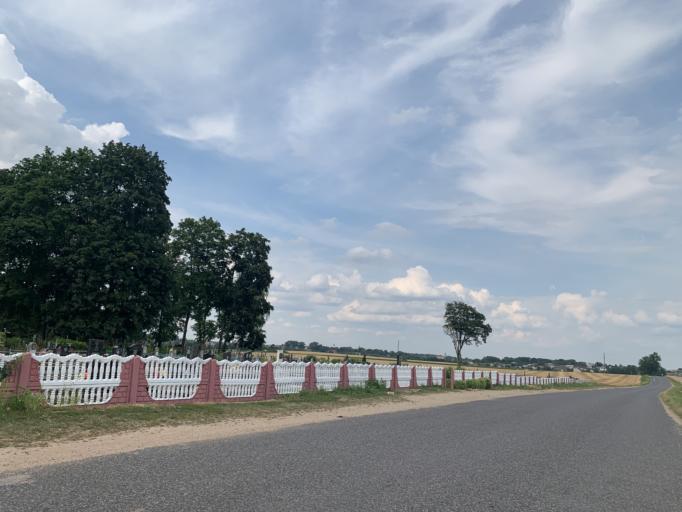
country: BY
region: Minsk
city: Nyasvizh
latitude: 53.1998
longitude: 26.6721
